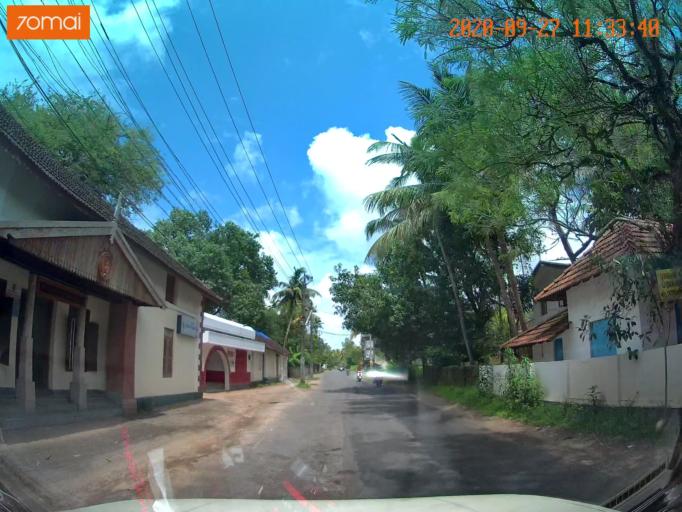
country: IN
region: Kerala
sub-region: Thrissur District
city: Thanniyam
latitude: 10.4325
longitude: 76.1285
